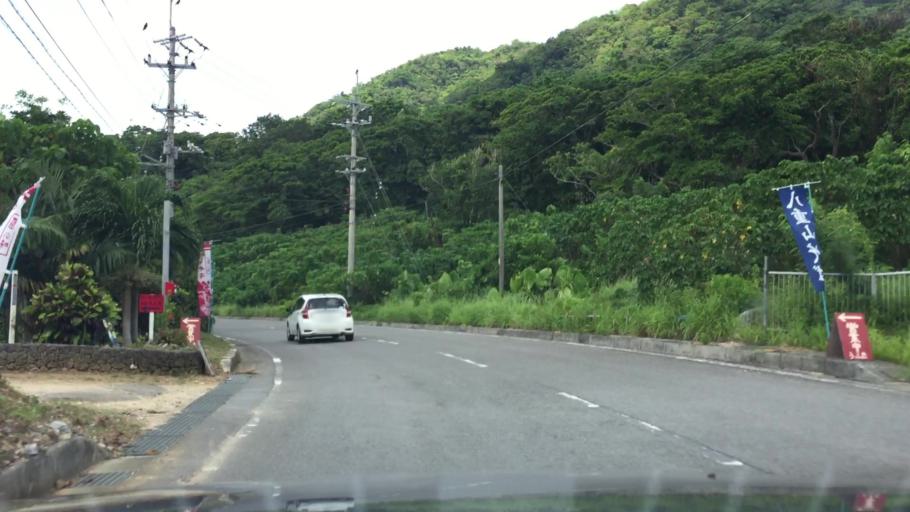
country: JP
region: Okinawa
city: Ishigaki
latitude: 24.4571
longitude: 124.2266
